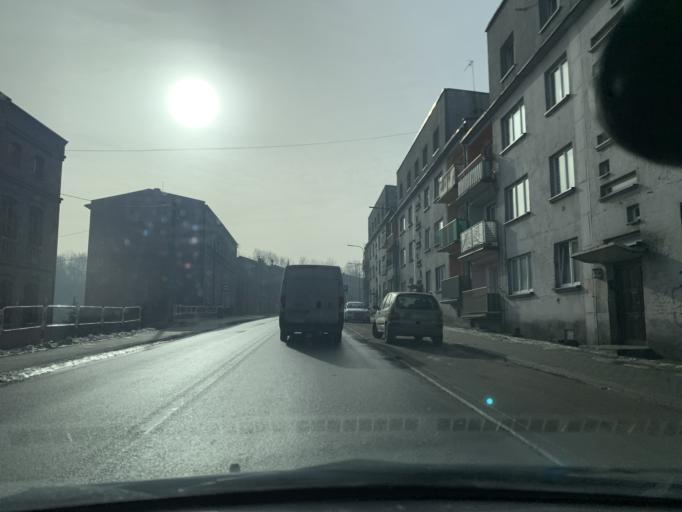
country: PL
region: Silesian Voivodeship
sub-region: Ruda Slaska
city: Ruda Slaska
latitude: 50.3233
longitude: 18.8565
